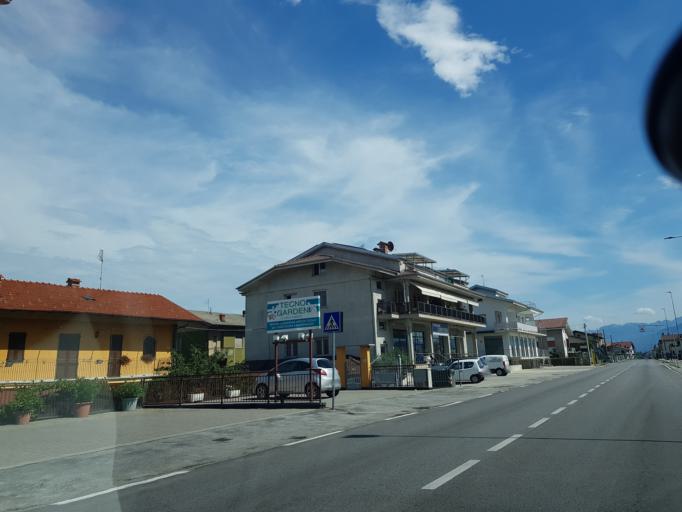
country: IT
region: Piedmont
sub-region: Provincia di Cuneo
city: Tarantasca
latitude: 44.4810
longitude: 7.5048
